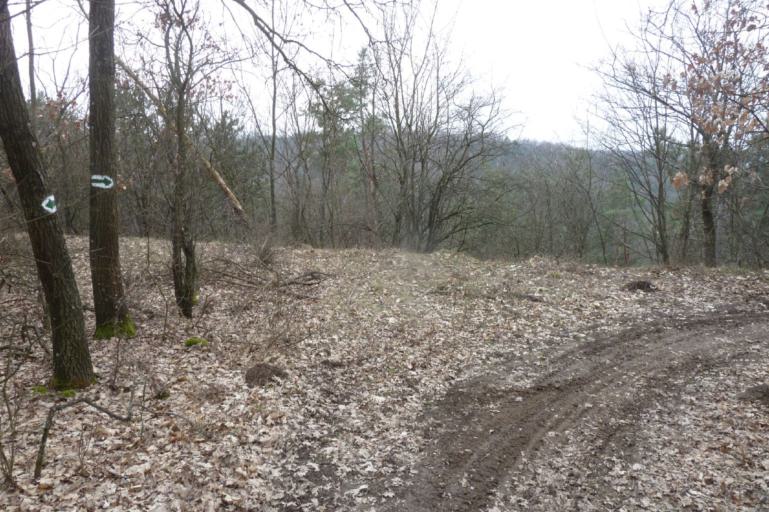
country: HU
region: Pest
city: Pecel
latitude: 47.4896
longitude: 19.3605
